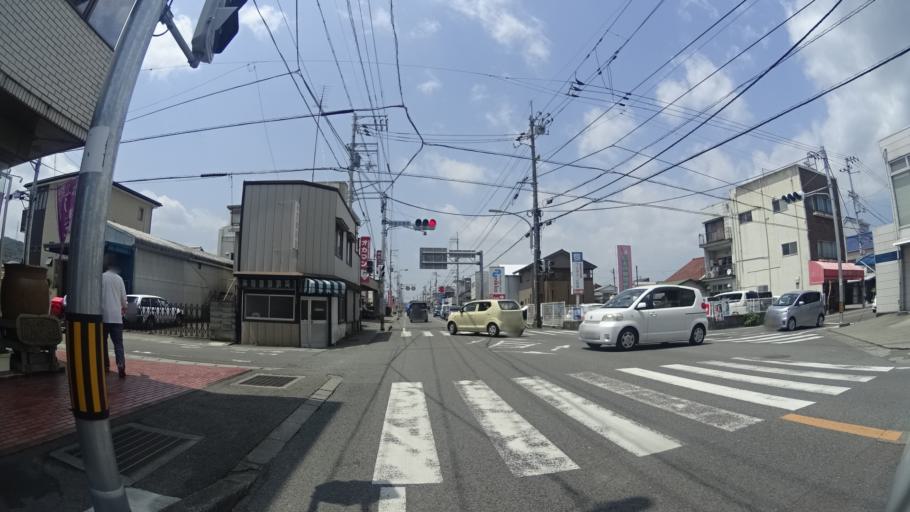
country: JP
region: Tokushima
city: Ishii
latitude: 34.0679
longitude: 134.4428
